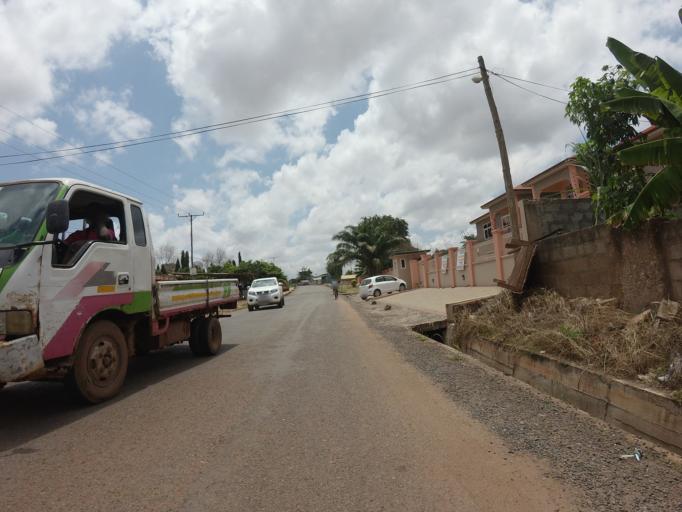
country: GH
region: Greater Accra
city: Medina Estates
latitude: 5.6810
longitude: -0.1965
